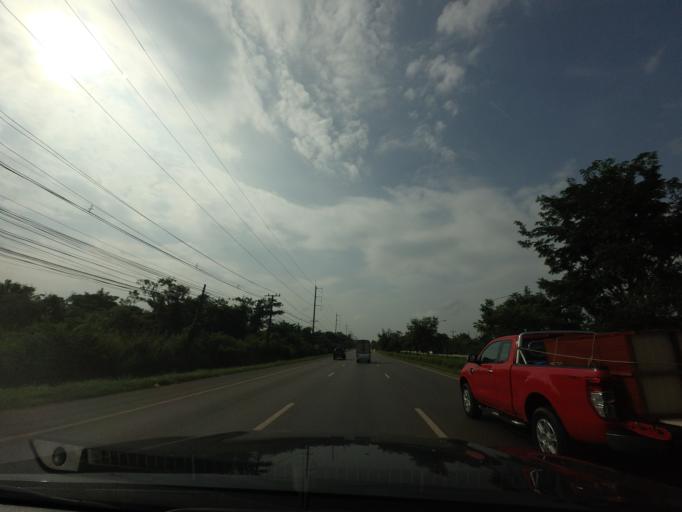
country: TH
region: Nong Khai
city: Nong Khai
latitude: 17.8268
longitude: 102.7562
